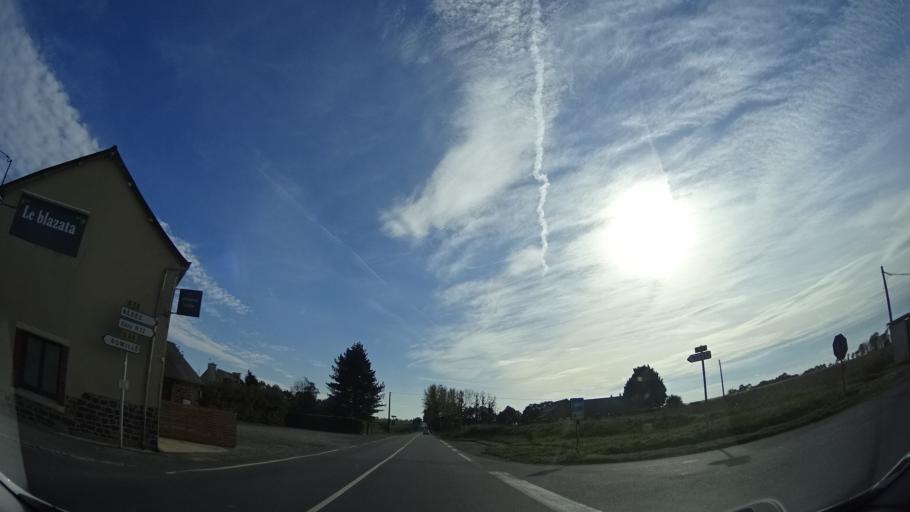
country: FR
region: Brittany
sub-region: Departement d'Ille-et-Vilaine
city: Bedee
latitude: 48.2084
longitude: -1.9415
